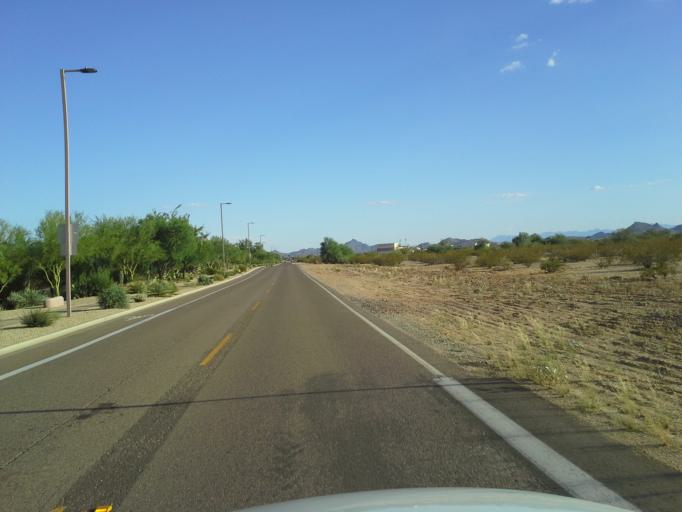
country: US
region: Arizona
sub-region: Maricopa County
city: Cave Creek
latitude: 33.6900
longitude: -112.0051
